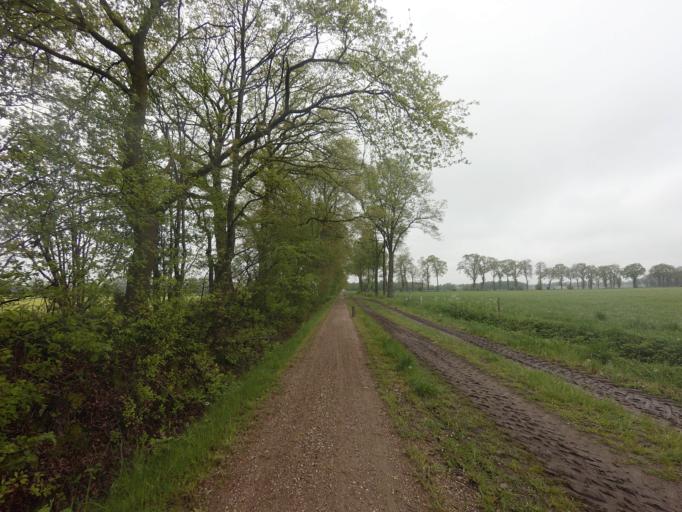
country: NL
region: Overijssel
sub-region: Gemeente Haaksbergen
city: Haaksbergen
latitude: 52.1289
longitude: 6.8140
